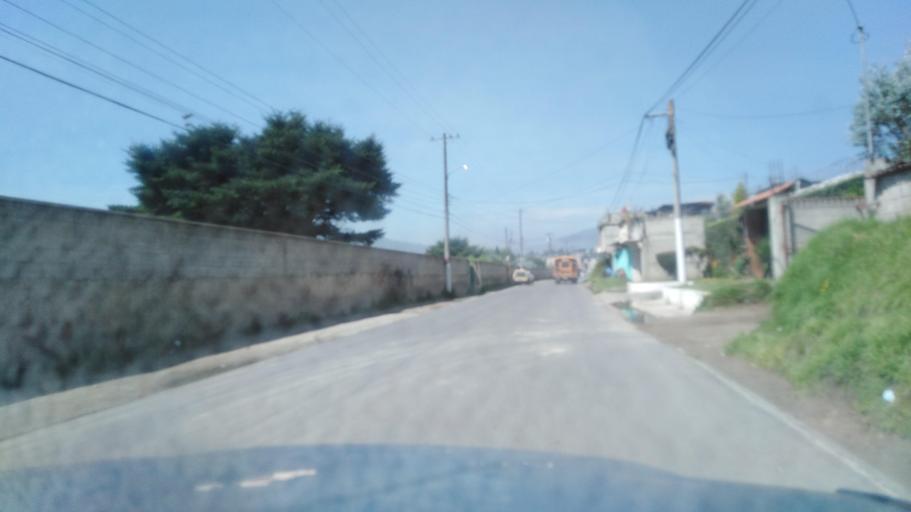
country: GT
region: Quetzaltenango
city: Quetzaltenango
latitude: 14.8537
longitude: -91.4931
